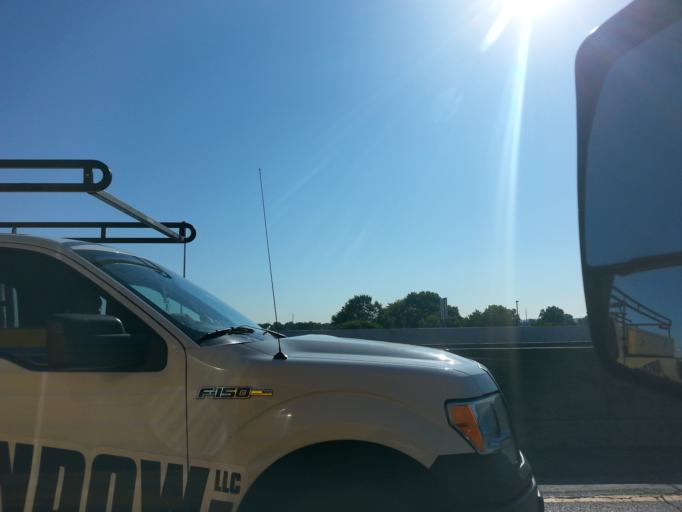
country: US
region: Indiana
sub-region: Clark County
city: Jeffersonville
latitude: 38.2715
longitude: -85.7472
